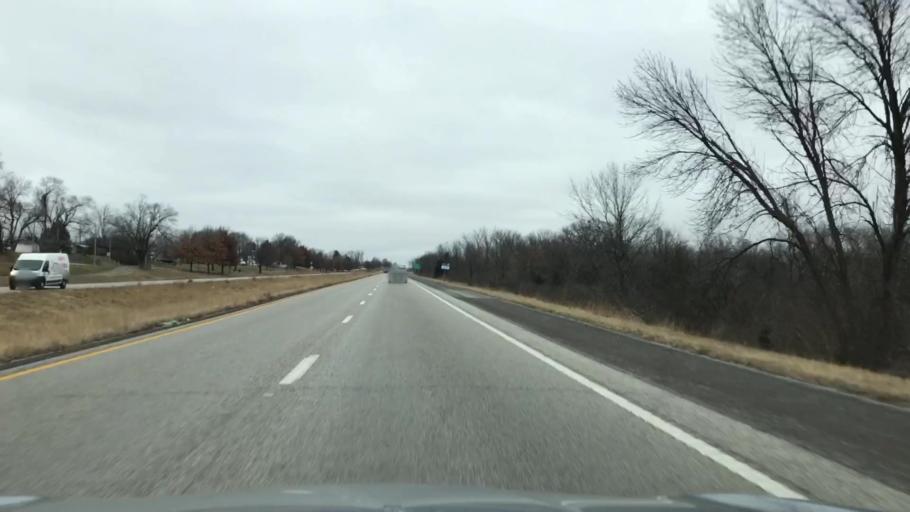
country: US
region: Missouri
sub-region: Clay County
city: Liberty
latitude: 39.2202
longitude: -94.4097
